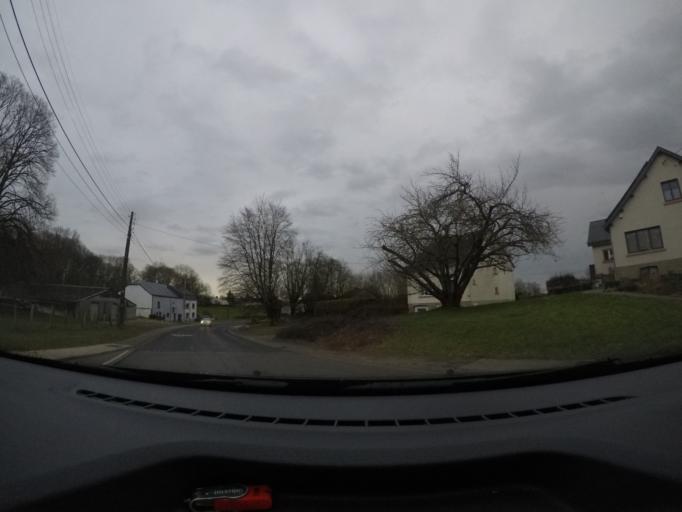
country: BE
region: Wallonia
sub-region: Province du Luxembourg
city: Tintigny
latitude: 49.6698
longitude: 5.4947
